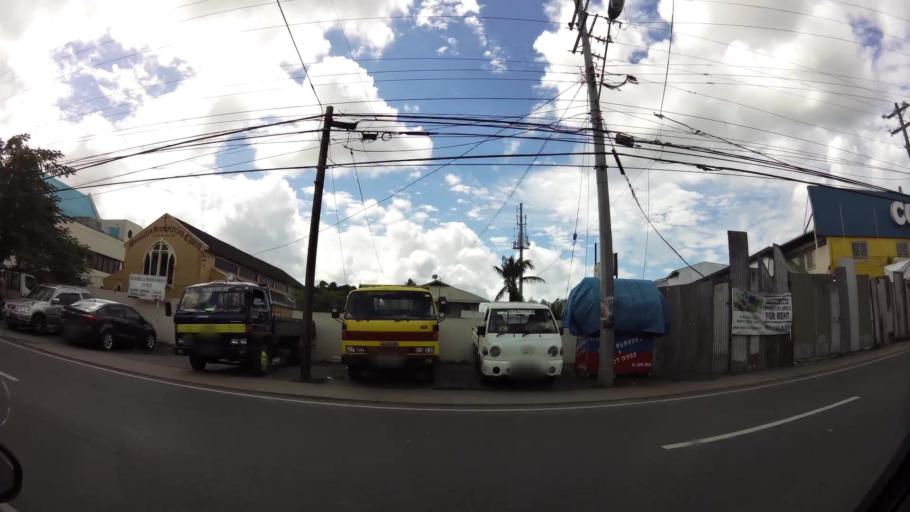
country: TT
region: City of San Fernando
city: Marabella
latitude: 10.3033
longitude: -61.4502
